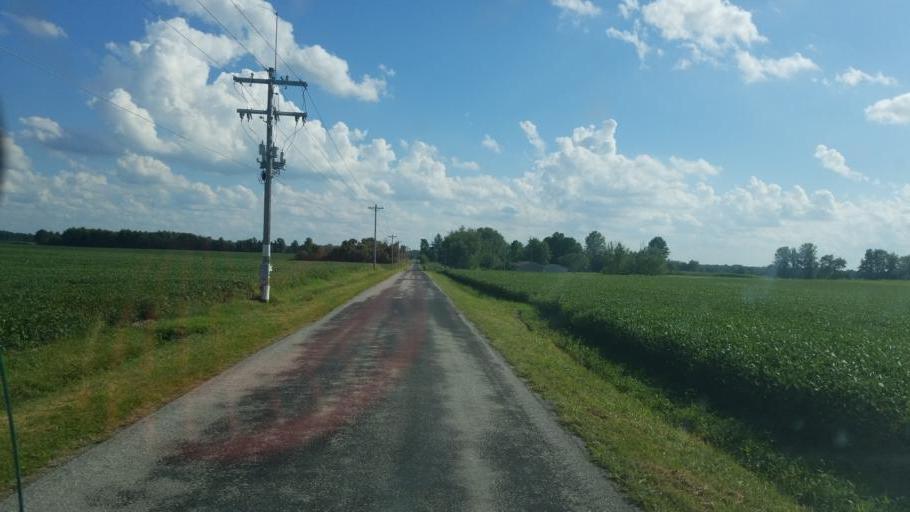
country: US
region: Ohio
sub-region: Union County
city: Richwood
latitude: 40.5966
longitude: -83.3617
